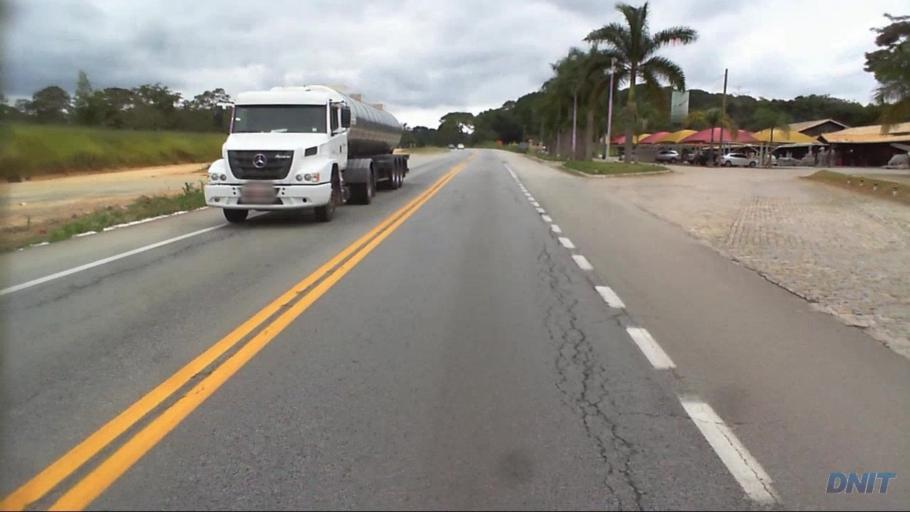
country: BR
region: Minas Gerais
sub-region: Barao De Cocais
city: Barao de Cocais
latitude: -19.7687
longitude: -43.4519
